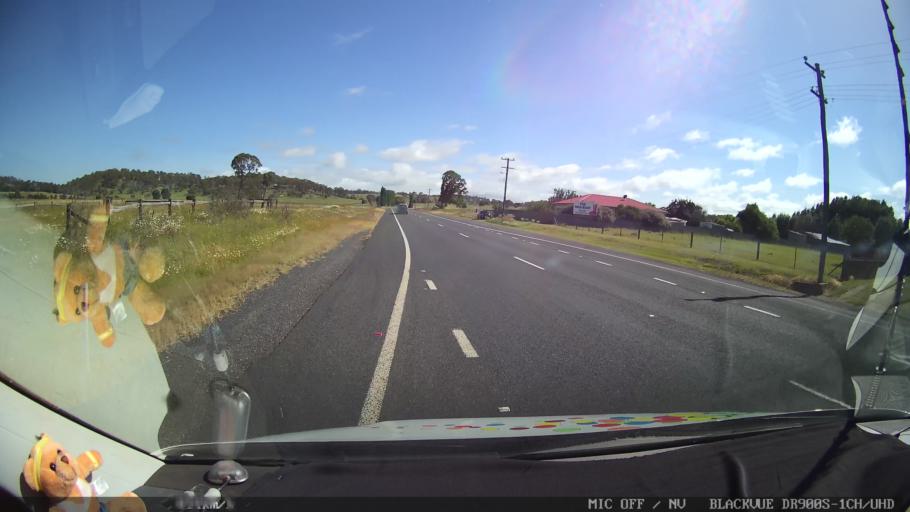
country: AU
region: New South Wales
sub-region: Guyra
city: Guyra
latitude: -30.1285
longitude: 151.6838
